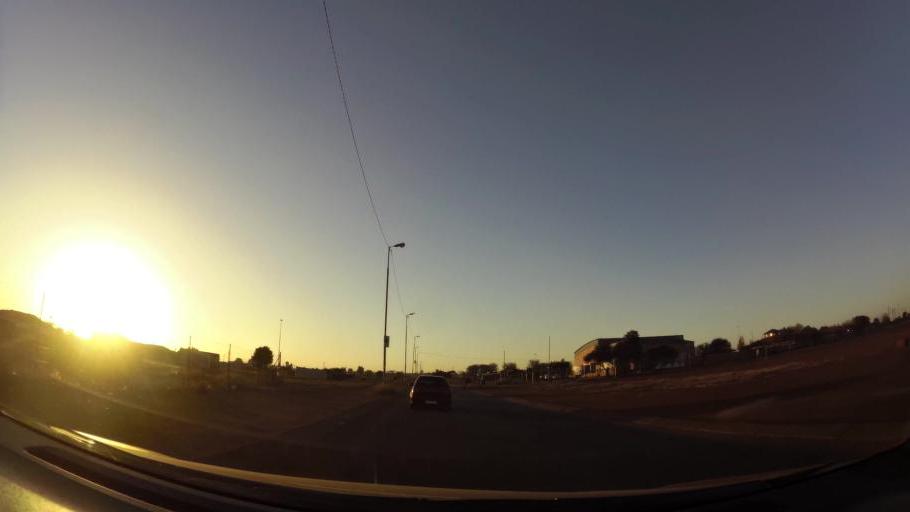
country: ZA
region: Gauteng
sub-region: City of Tshwane Metropolitan Municipality
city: Mabopane
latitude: -25.5855
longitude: 28.0892
